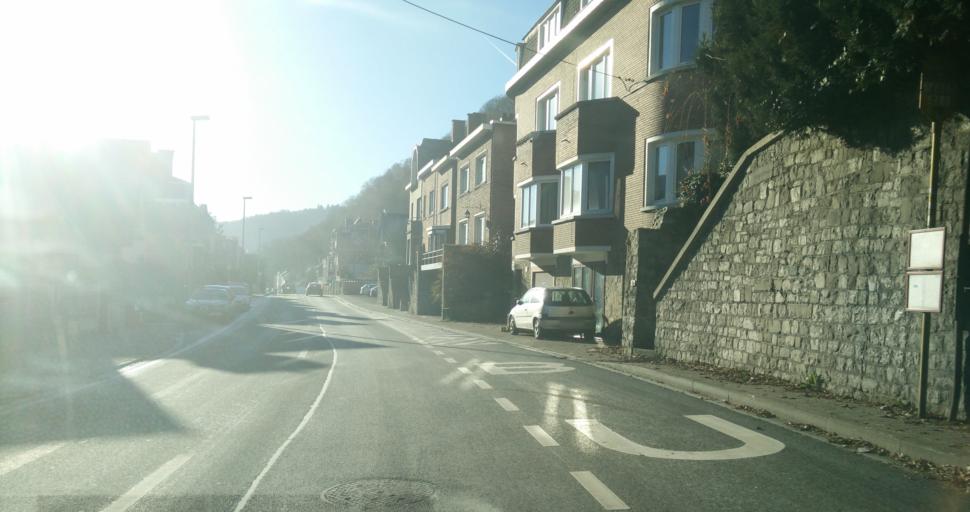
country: BE
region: Wallonia
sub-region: Province de Namur
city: Namur
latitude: 50.4506
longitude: 4.8568
